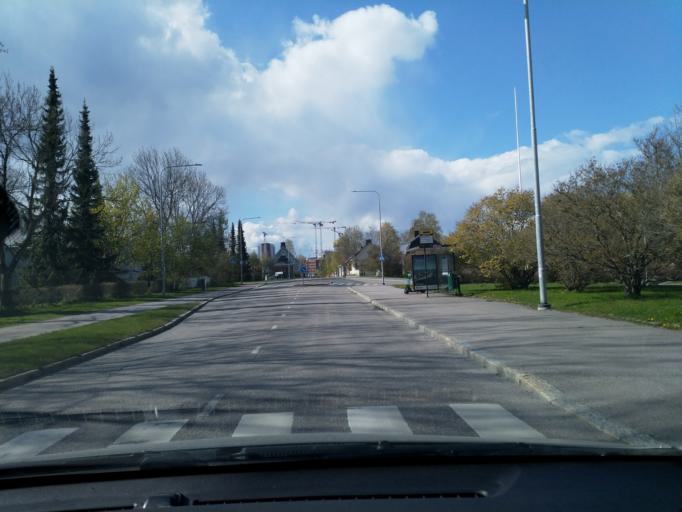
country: FI
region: Pirkanmaa
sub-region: Tampere
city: Tampere
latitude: 61.4863
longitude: 23.7847
